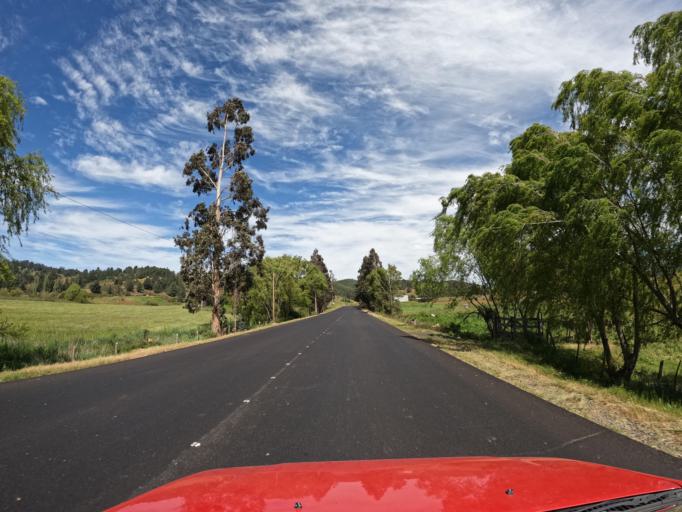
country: CL
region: Maule
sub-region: Provincia de Talca
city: Constitucion
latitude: -35.0577
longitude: -72.0400
